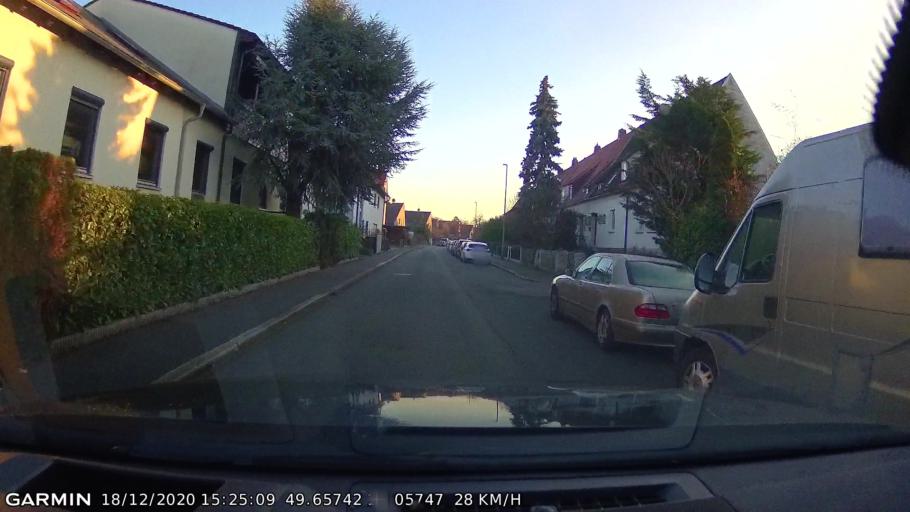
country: DE
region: Bavaria
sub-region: Upper Franconia
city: Poxdorf
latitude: 49.6574
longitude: 11.0575
